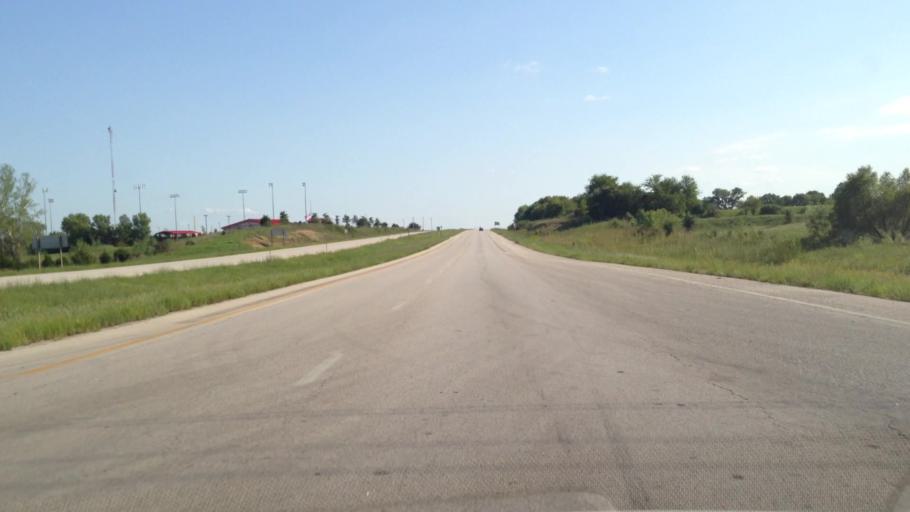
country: US
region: Kansas
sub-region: Bourbon County
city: Fort Scott
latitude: 37.7905
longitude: -94.7048
